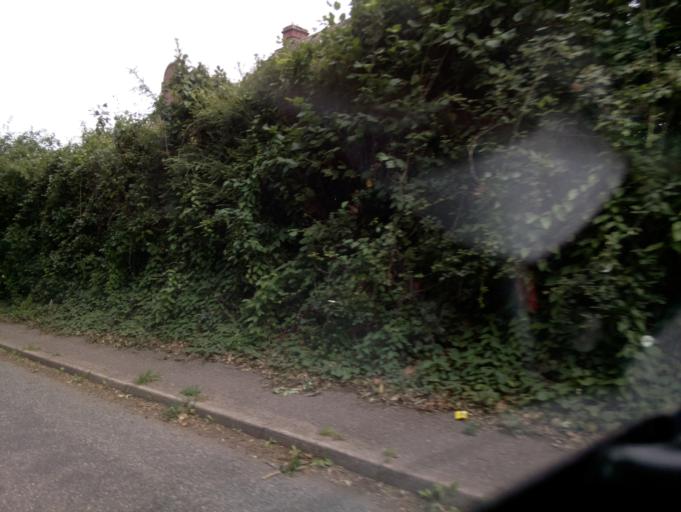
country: GB
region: England
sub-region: Devon
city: Bradninch
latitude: 50.7672
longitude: -3.4428
